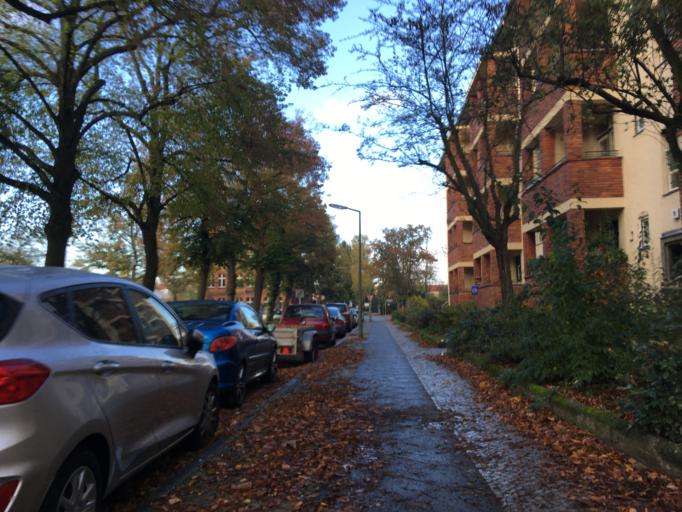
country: DE
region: Berlin
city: Wedding Bezirk
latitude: 52.5635
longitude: 13.3720
